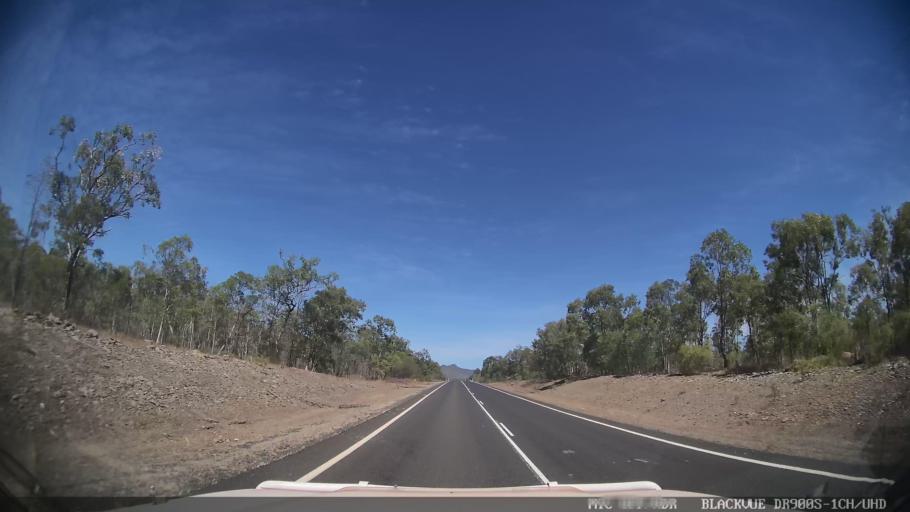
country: AU
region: Queensland
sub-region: Cook
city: Cooktown
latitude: -15.7031
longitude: 144.6077
